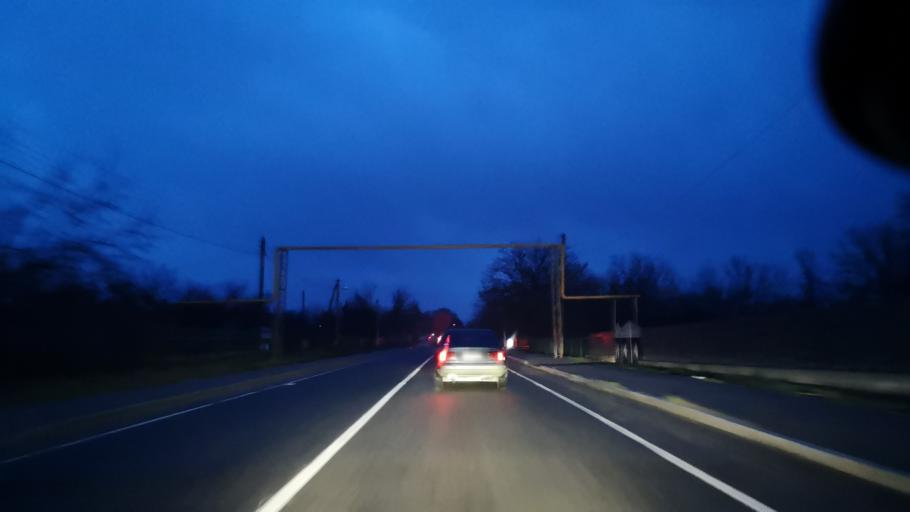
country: MD
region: Orhei
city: Orhei
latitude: 47.4357
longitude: 28.7978
